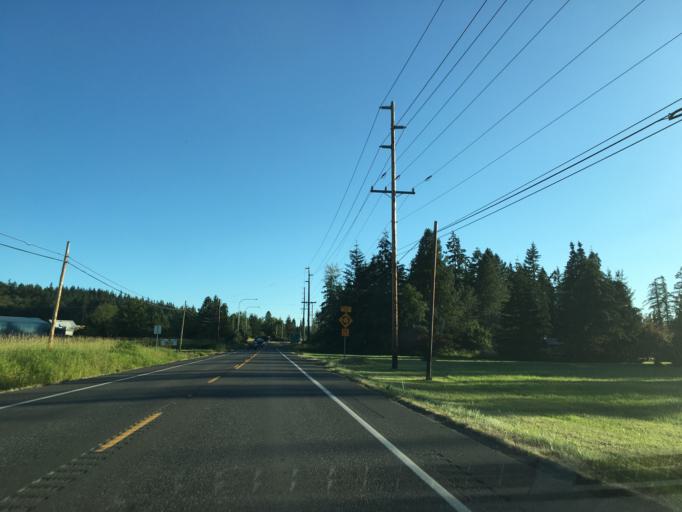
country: US
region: Washington
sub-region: Whatcom County
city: Everson
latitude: 48.8344
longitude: -122.3029
